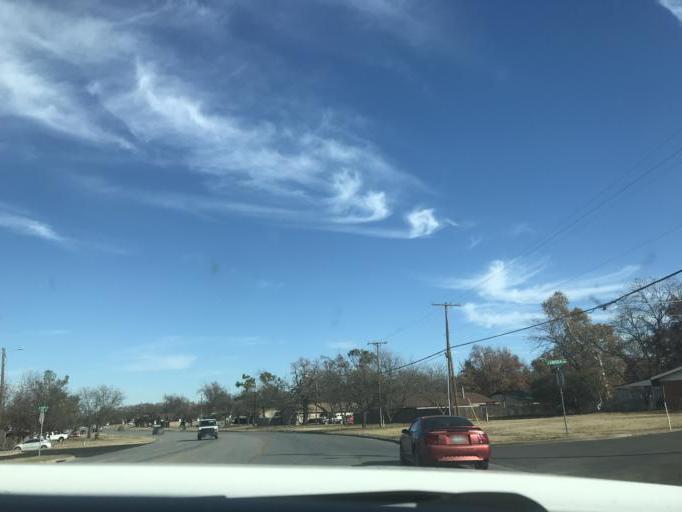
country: US
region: Texas
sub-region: Erath County
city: Stephenville
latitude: 32.2248
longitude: -98.2253
